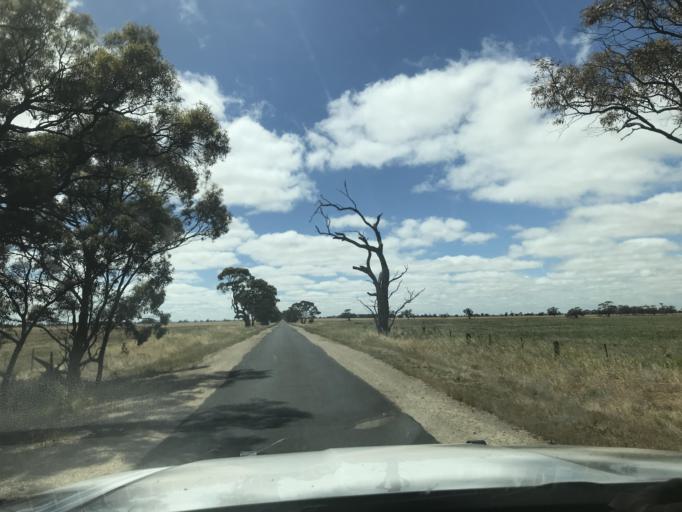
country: AU
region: South Australia
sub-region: Tatiara
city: Bordertown
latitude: -36.2771
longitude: 141.1018
